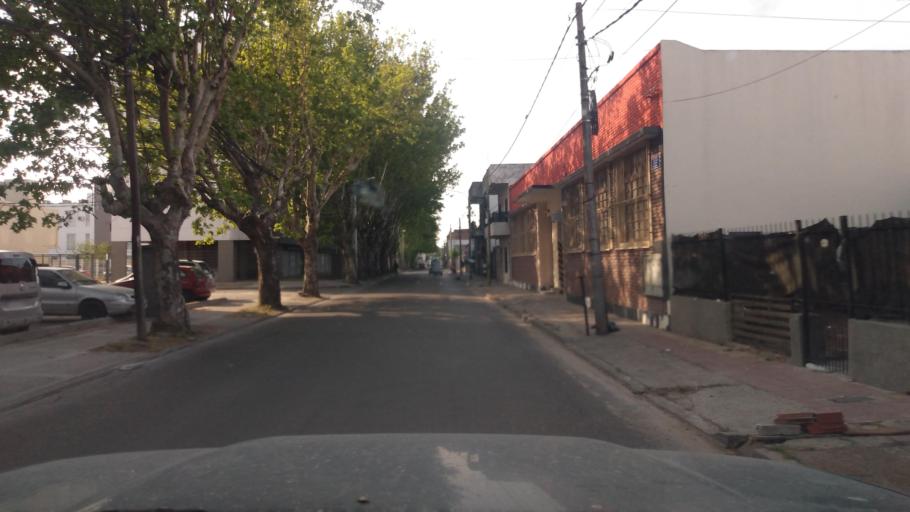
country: AR
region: Buenos Aires
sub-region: Partido de Moron
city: Moron
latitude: -34.6525
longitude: -58.6024
